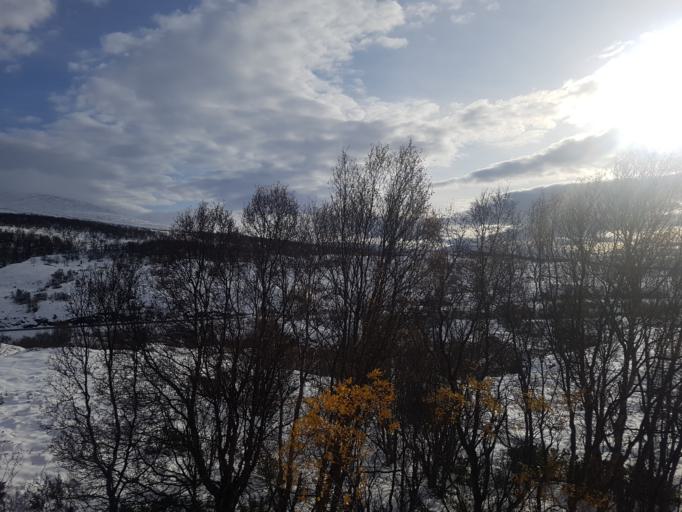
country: NO
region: Sor-Trondelag
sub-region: Oppdal
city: Oppdal
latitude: 62.2788
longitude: 9.5881
